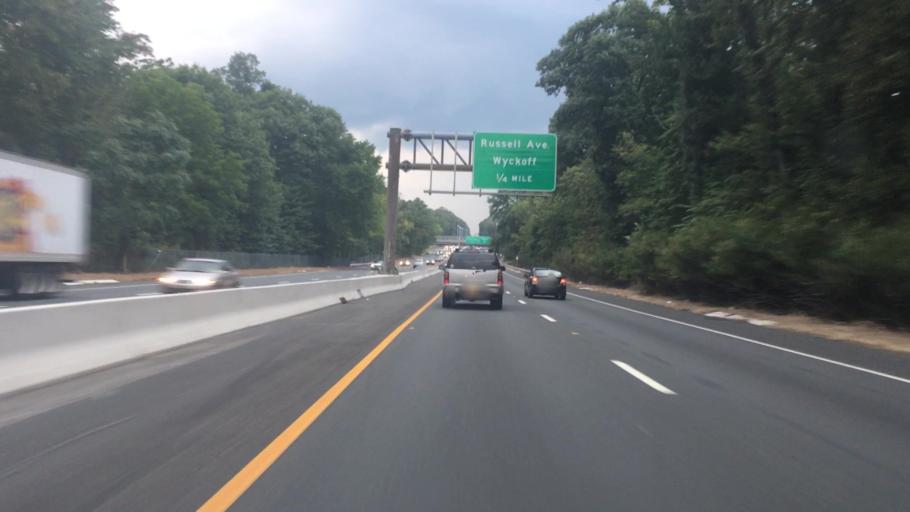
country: US
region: New Jersey
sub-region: Bergen County
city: Wyckoff
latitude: 40.9944
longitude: -74.1767
